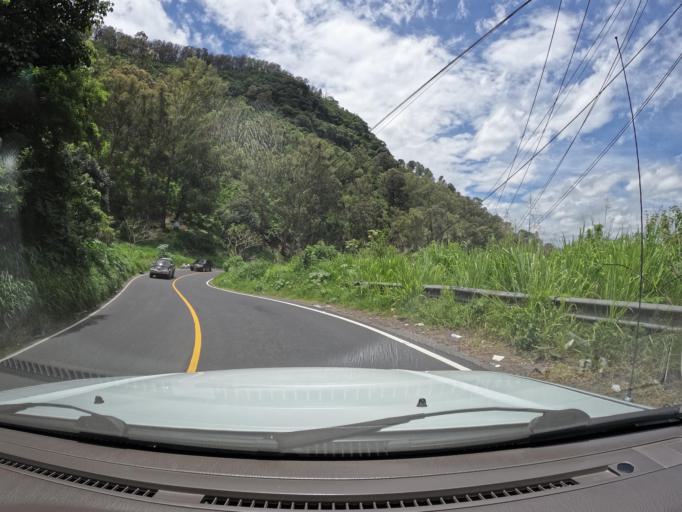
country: GT
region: Guatemala
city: Amatitlan
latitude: 14.4942
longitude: -90.6223
